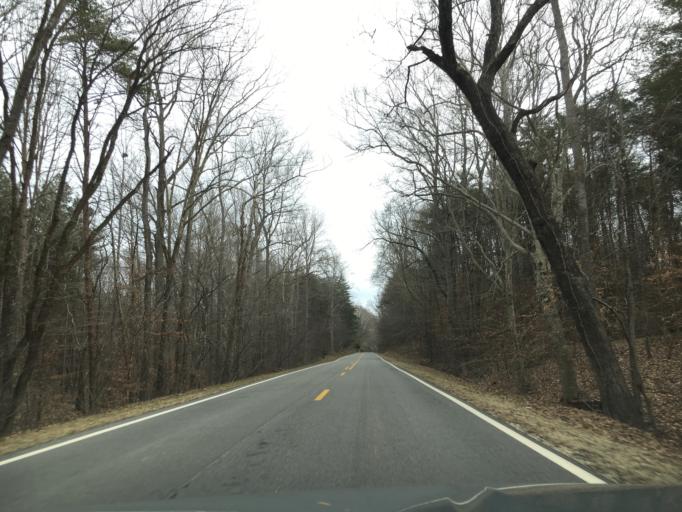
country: US
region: Virginia
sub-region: Charlotte County
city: Charlotte Court House
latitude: 37.1481
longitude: -78.7563
